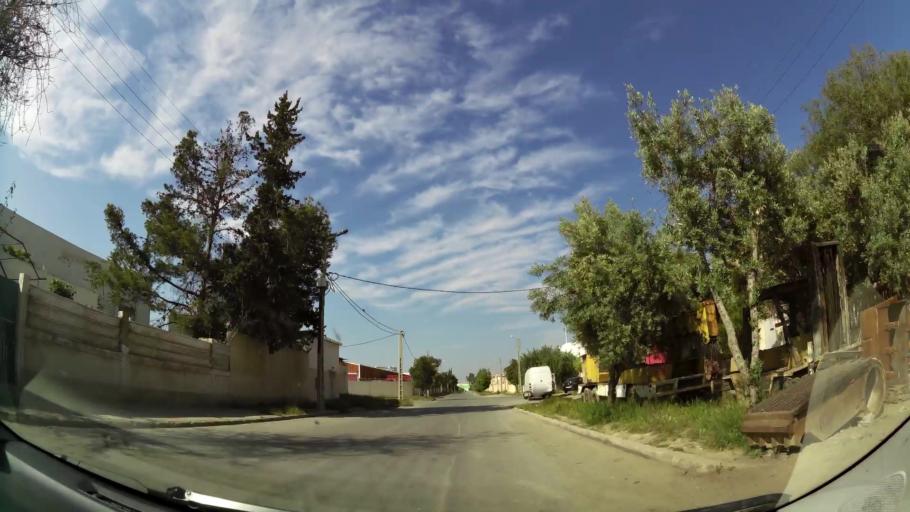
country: MA
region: Oriental
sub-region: Oujda-Angad
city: Oujda
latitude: 34.7040
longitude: -1.8906
